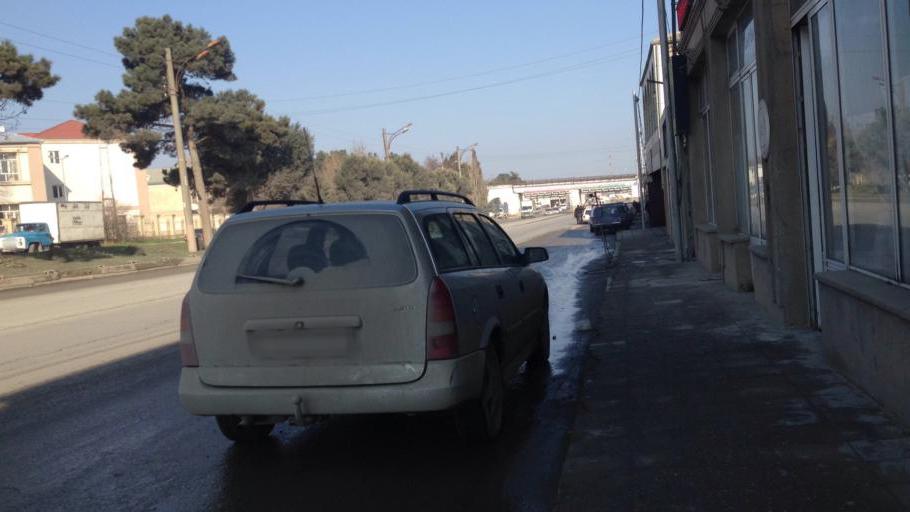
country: AZ
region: Baki
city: Binagadi
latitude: 40.4377
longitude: 49.8447
